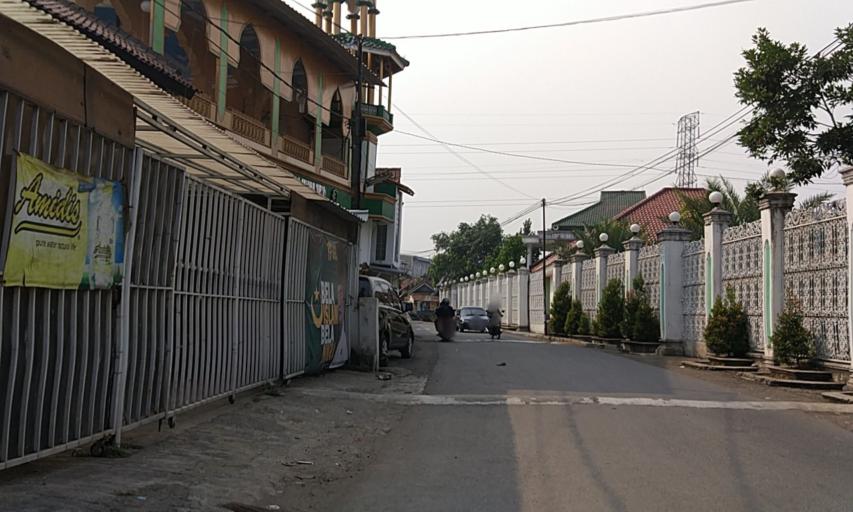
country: ID
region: West Java
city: Margahayukencana
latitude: -6.9673
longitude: 107.5597
